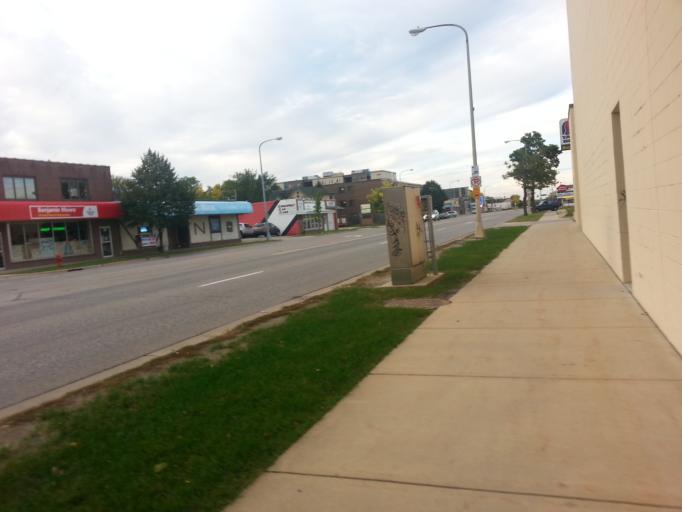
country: US
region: Minnesota
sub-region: Olmsted County
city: Rochester
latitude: 44.0280
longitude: -92.4629
